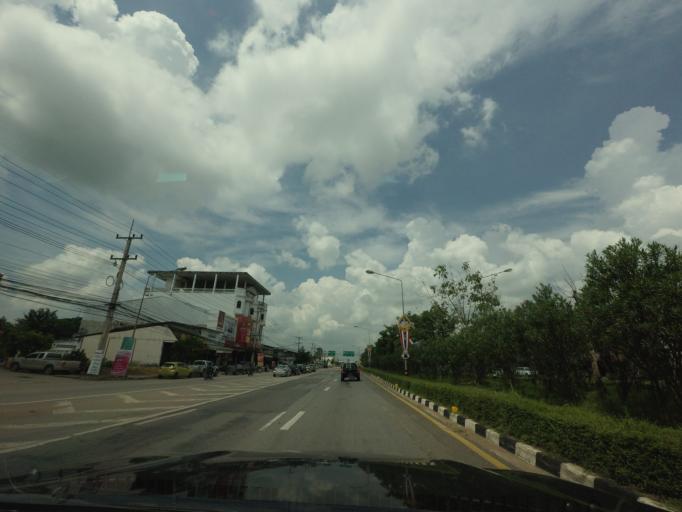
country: TH
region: Khon Kaen
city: Nong Ruea
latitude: 16.4911
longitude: 102.4379
